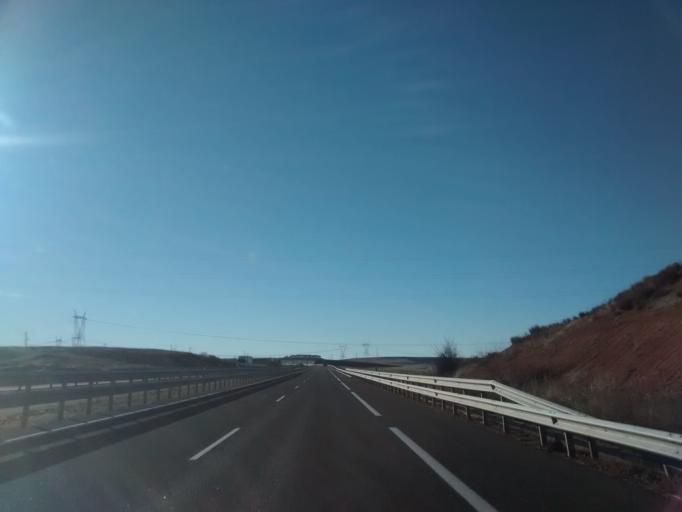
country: ES
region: Castille and Leon
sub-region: Provincia de Palencia
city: Herrera de Pisuerga
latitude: 42.5990
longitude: -4.3498
